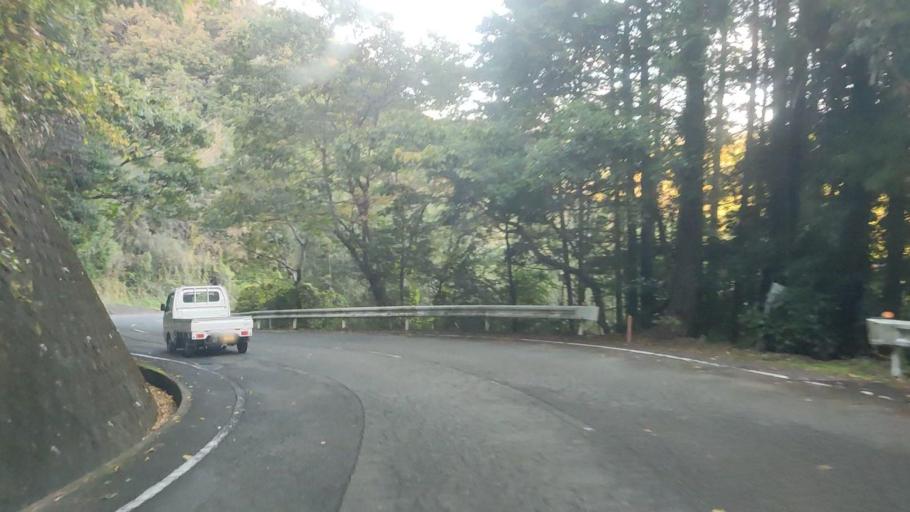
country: JP
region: Shizuoka
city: Mishima
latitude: 35.1327
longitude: 138.9805
